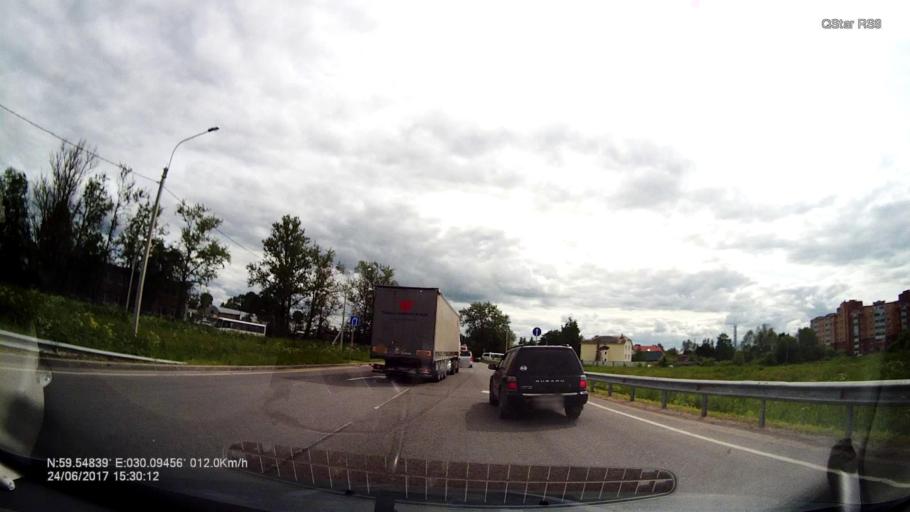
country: RU
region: Leningrad
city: Mariyenburg
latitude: 59.5483
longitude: 30.0948
